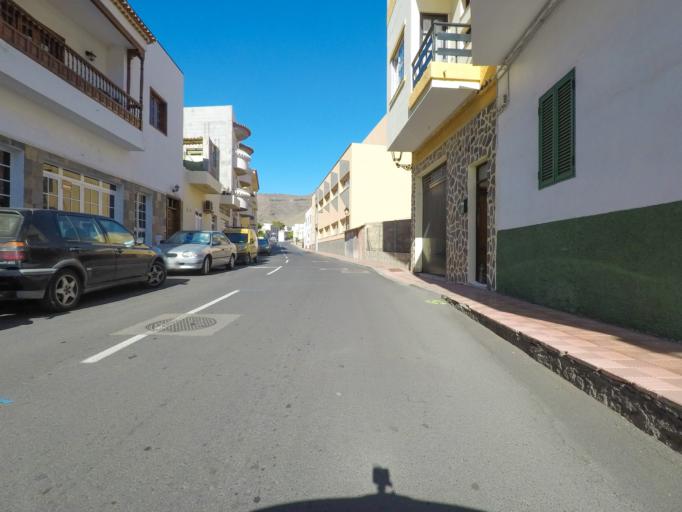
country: ES
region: Canary Islands
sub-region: Provincia de Santa Cruz de Tenerife
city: Alajero
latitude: 28.0307
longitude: -17.1979
